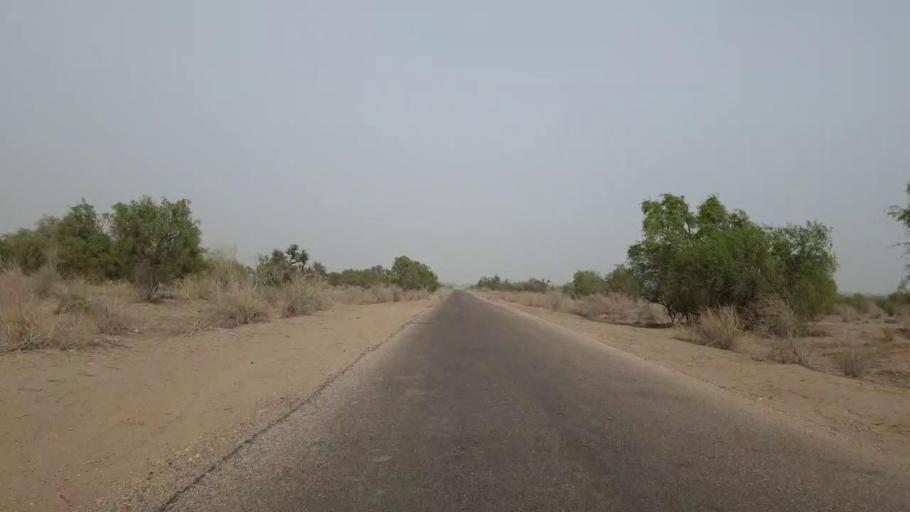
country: PK
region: Sindh
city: Islamkot
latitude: 24.5699
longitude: 70.3233
